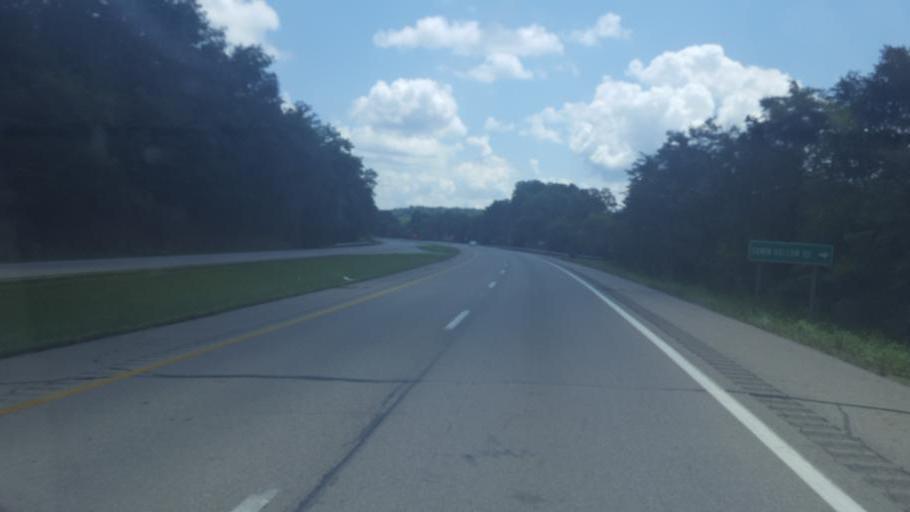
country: US
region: Ohio
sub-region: Jackson County
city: Jackson
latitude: 39.1341
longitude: -82.7151
